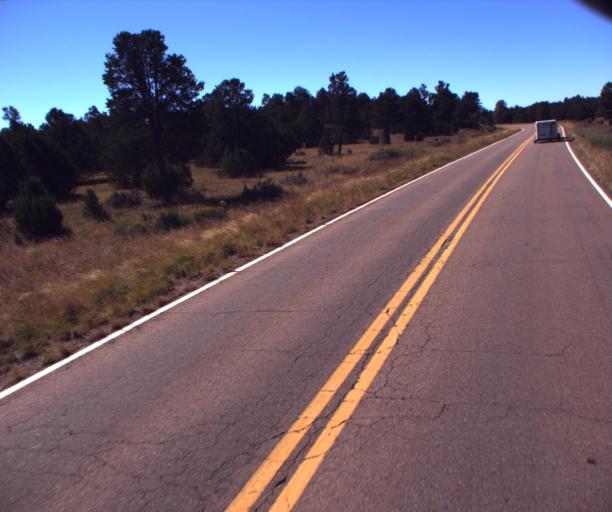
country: US
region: Arizona
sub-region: Navajo County
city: Heber-Overgaard
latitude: 34.4486
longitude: -110.5274
